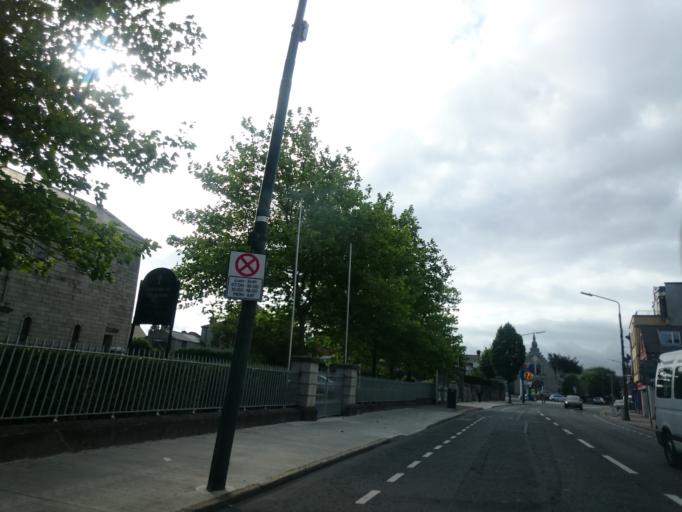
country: IE
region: Leinster
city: Rathgar
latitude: 53.3209
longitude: -6.2790
